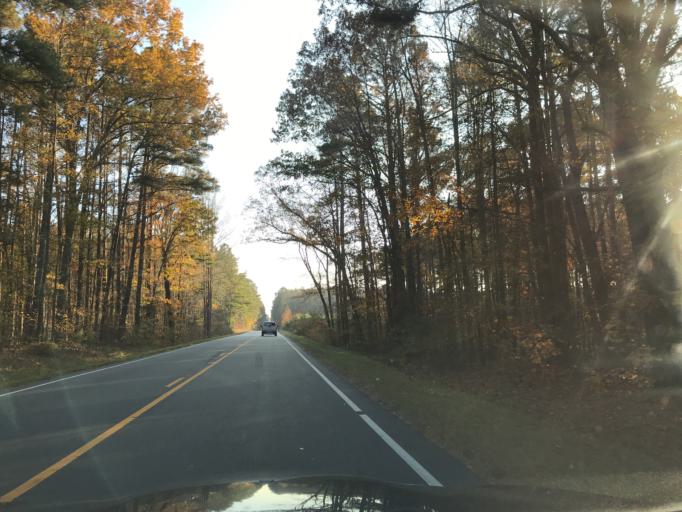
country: US
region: North Carolina
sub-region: Granville County
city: Creedmoor
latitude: 36.0883
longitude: -78.6914
